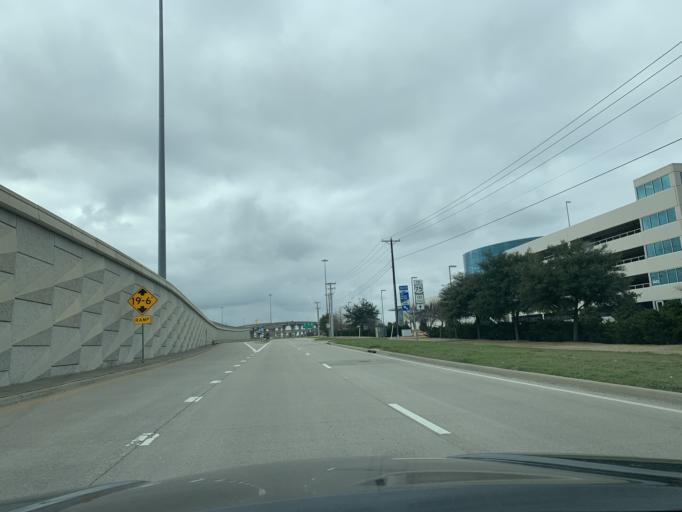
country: US
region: Texas
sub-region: Collin County
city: Fairview
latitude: 33.1624
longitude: -96.6372
